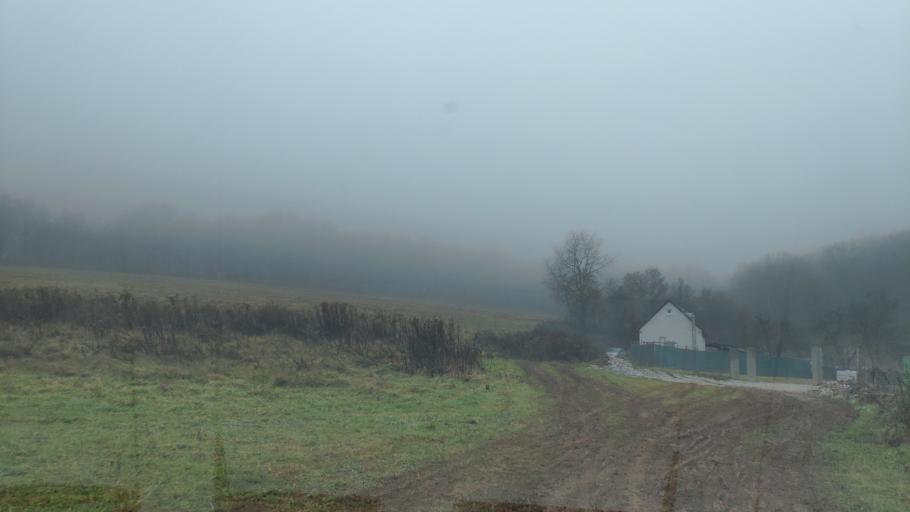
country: SK
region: Banskobystricky
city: Revuca
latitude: 48.6517
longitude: 20.2573
